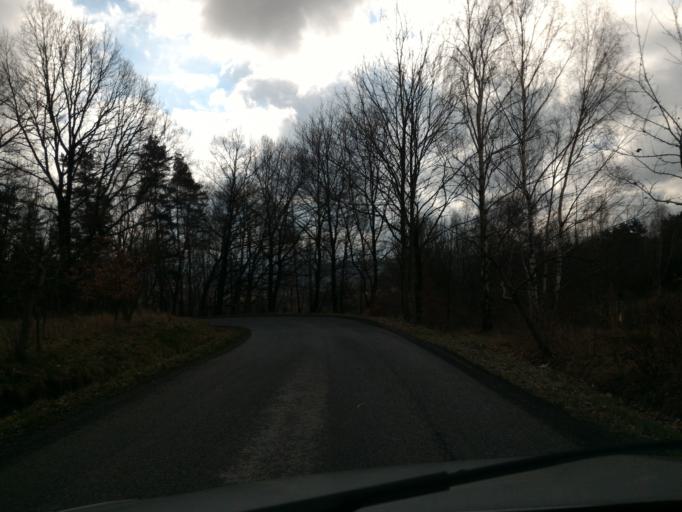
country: CZ
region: Liberecky
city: Visnova
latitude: 50.9928
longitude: 15.0198
